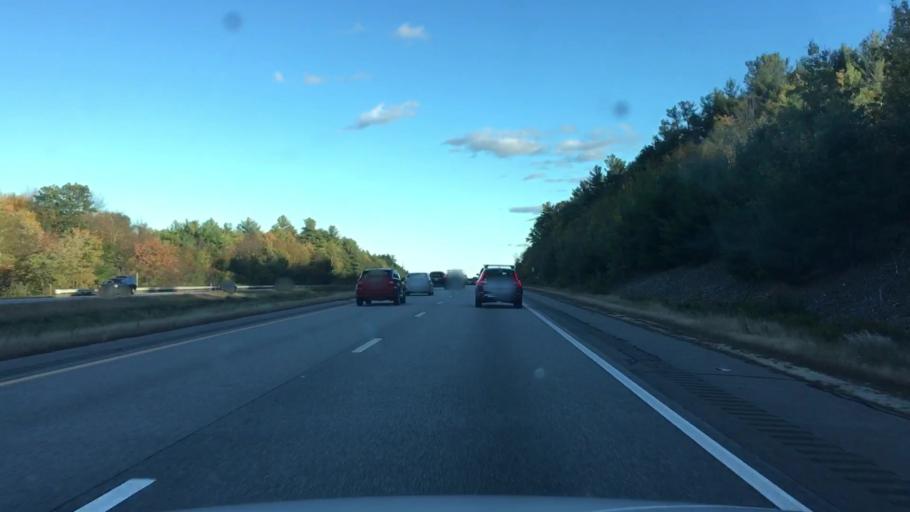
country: US
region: New Hampshire
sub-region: Rockingham County
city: Raymond
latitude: 43.0264
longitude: -71.2397
